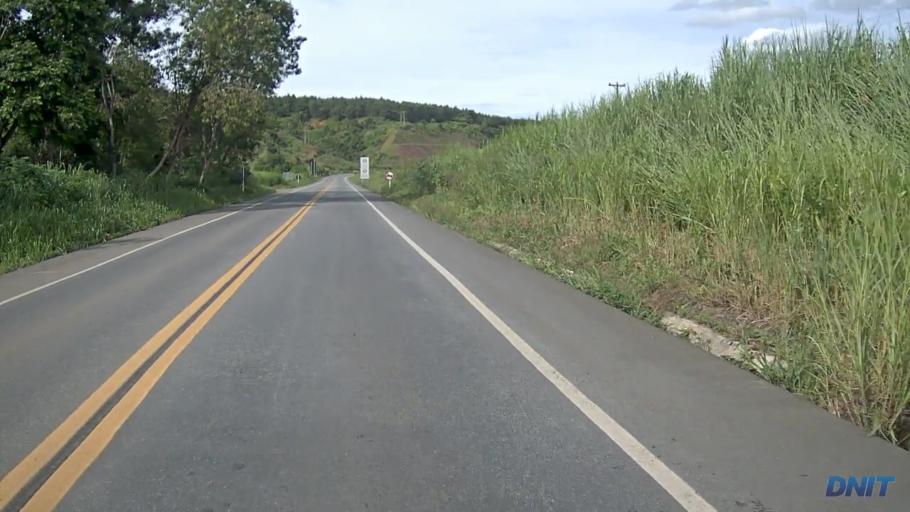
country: BR
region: Minas Gerais
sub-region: Belo Oriente
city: Belo Oriente
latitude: -19.2682
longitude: -42.3550
